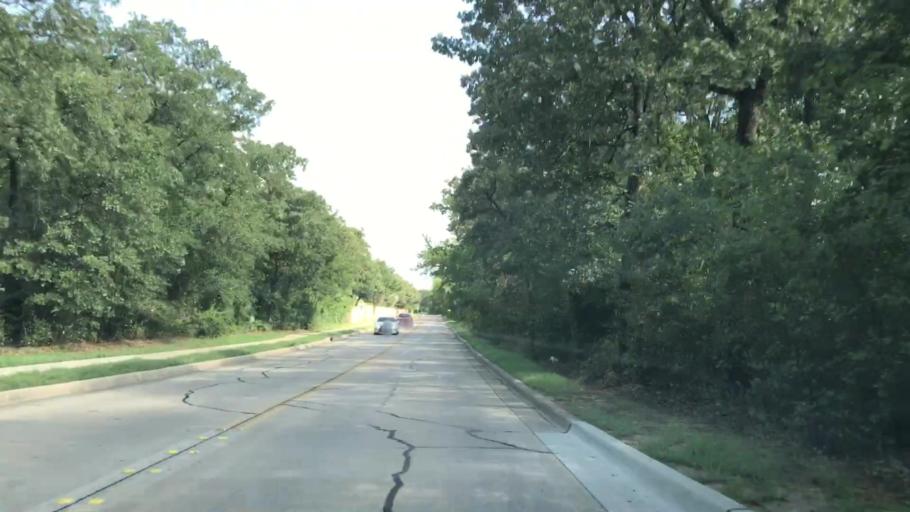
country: US
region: Texas
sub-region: Tarrant County
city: Keller
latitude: 32.9094
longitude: -97.2311
